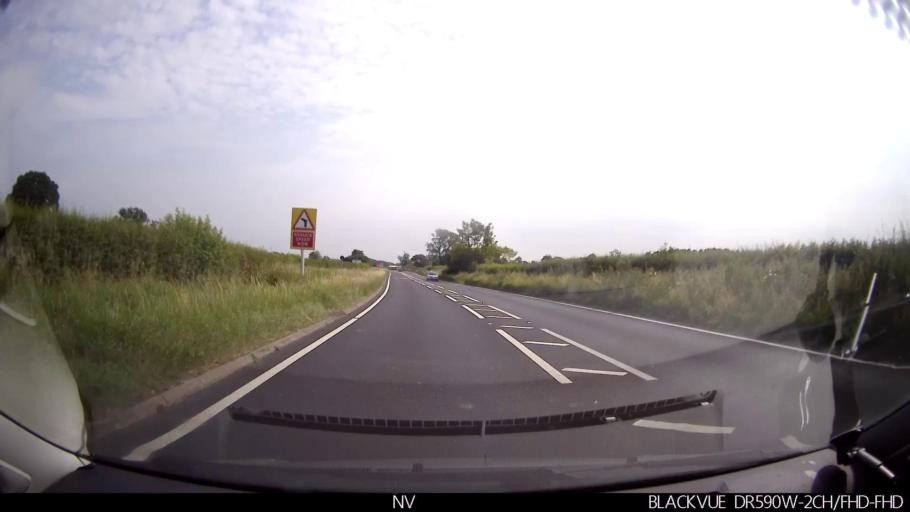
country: GB
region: England
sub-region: North Yorkshire
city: Huttons Ambo
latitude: 54.1179
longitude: -0.8349
